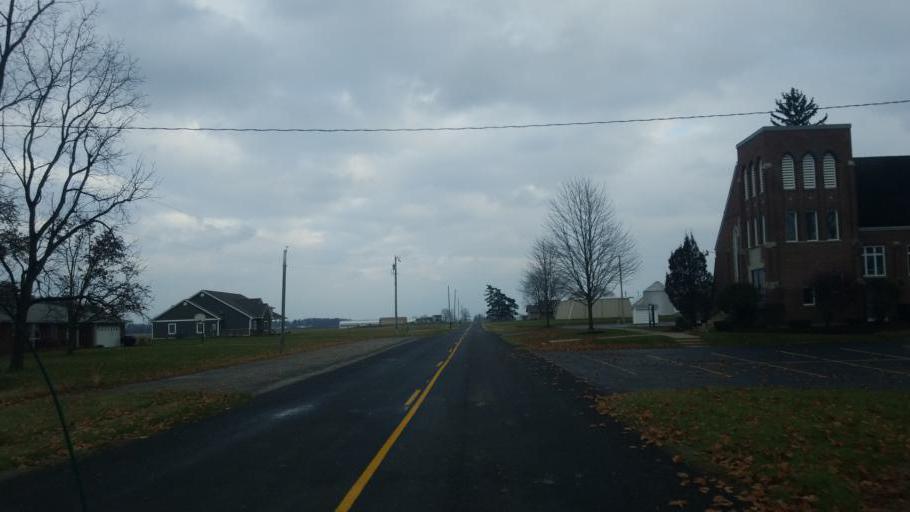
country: US
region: Ohio
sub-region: Mercer County
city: Fort Recovery
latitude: 40.5090
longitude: -84.7425
